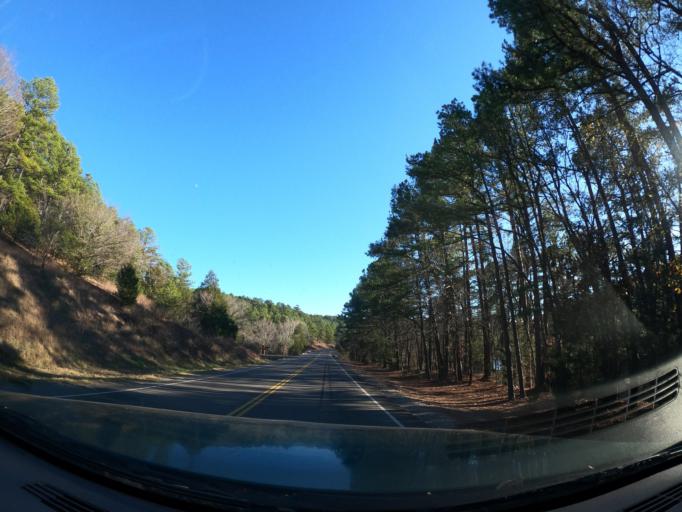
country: US
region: Oklahoma
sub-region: Latimer County
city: Wilburton
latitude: 34.9737
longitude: -95.3566
